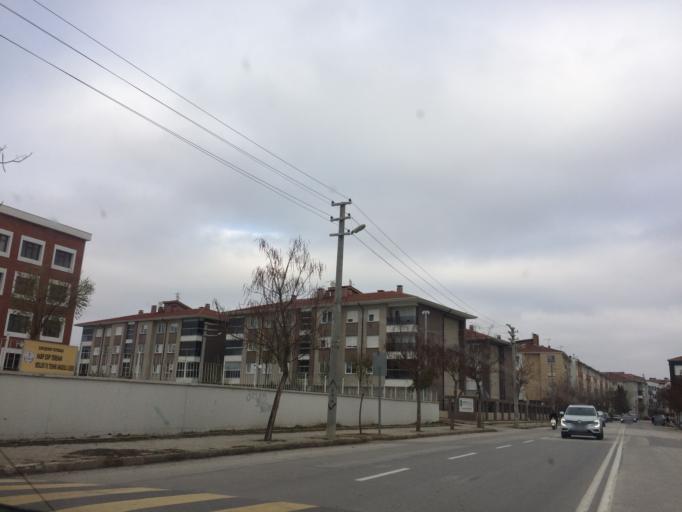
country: TR
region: Eskisehir
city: Eskisehir
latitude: 39.7791
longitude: 30.4859
